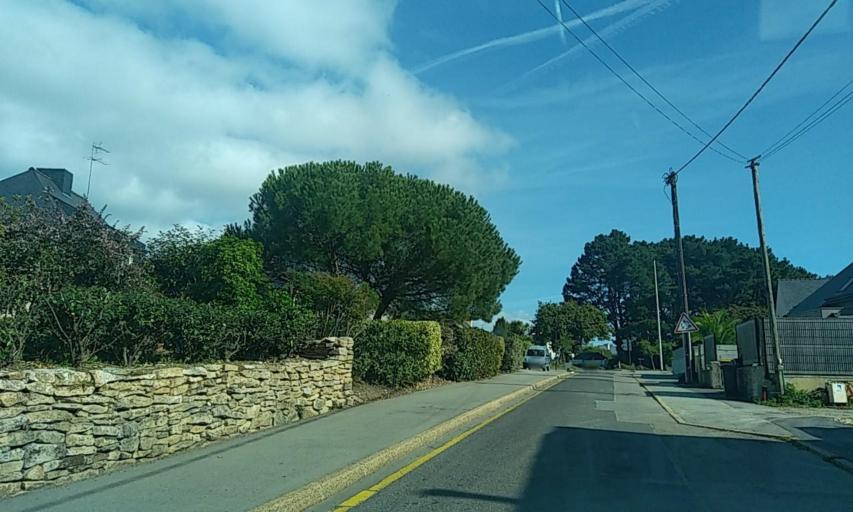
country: FR
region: Brittany
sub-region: Departement du Morbihan
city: Ploemeur
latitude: 47.7252
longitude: -3.4359
